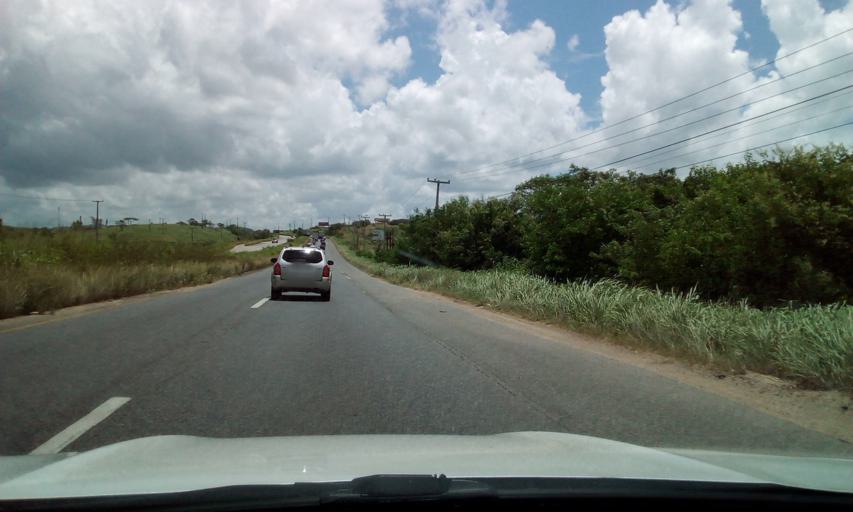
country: BR
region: Pernambuco
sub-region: Pombos
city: Pombos
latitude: -8.1305
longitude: -35.3608
